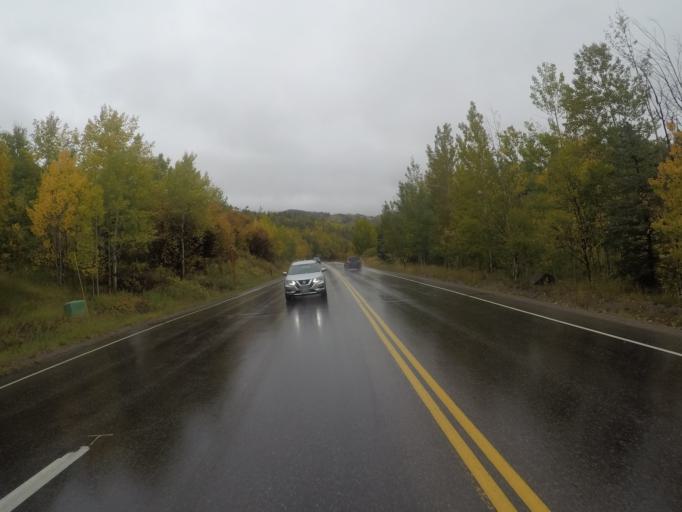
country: US
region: Colorado
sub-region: Pitkin County
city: Snowmass Village
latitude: 39.2131
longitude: -106.9398
